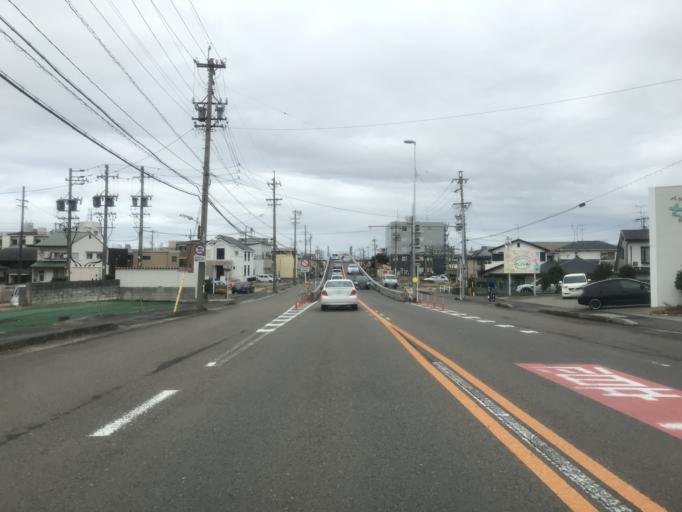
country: JP
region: Aichi
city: Nagoya-shi
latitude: 35.1936
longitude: 136.8667
